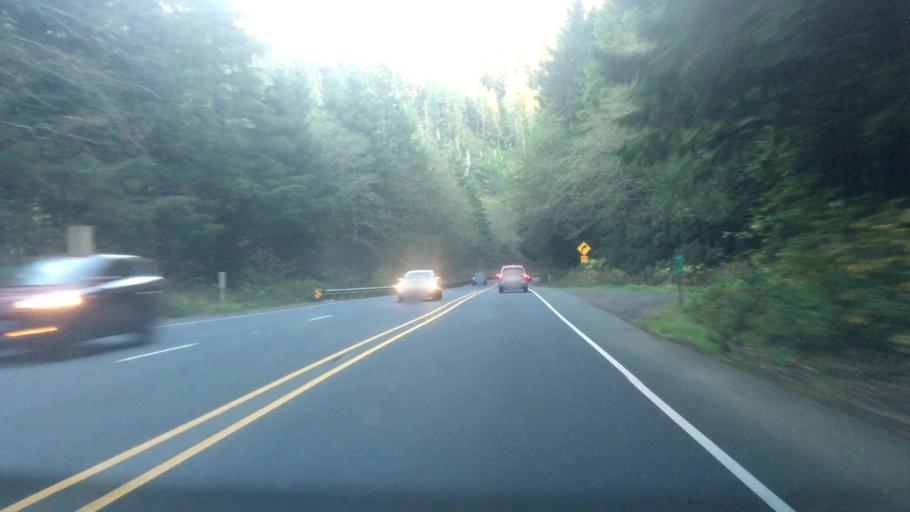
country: US
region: Oregon
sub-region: Clatsop County
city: Cannon Beach
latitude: 45.7753
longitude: -123.9455
